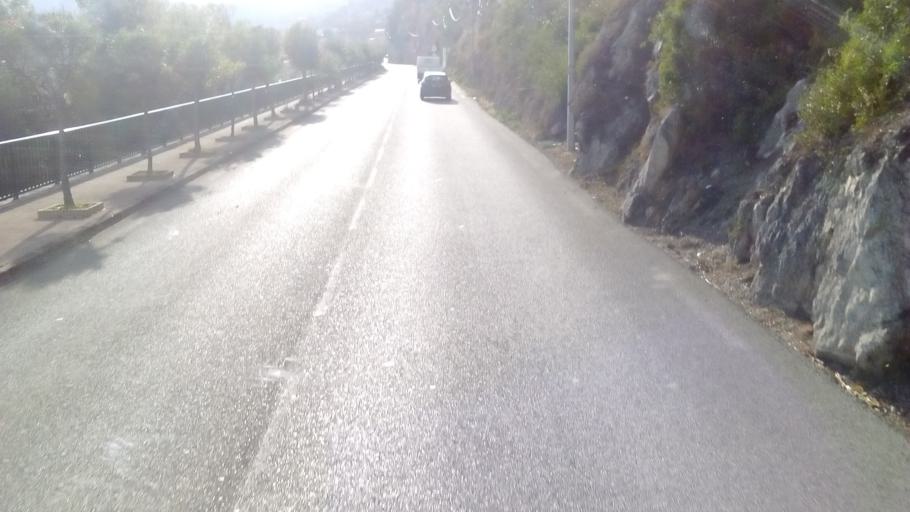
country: MC
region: Commune de Monaco
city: Saint-Roman
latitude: 43.7545
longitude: 7.4408
